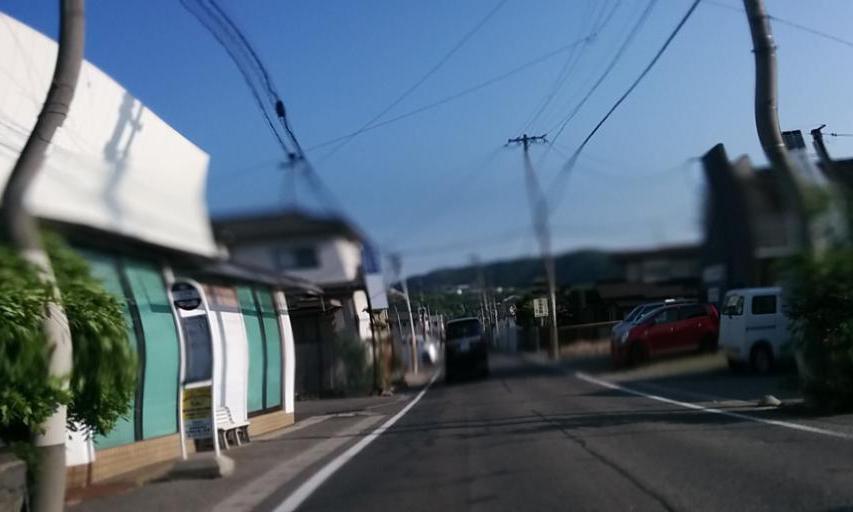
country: JP
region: Nagano
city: Matsumoto
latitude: 36.2215
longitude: 137.9863
